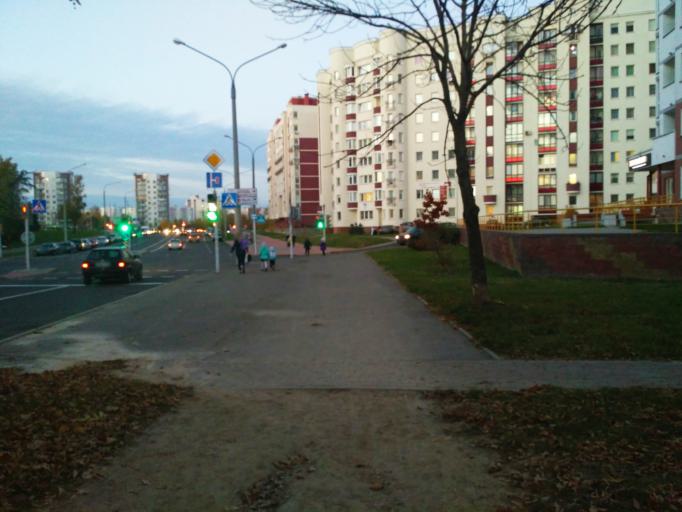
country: BY
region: Minsk
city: Novoye Medvezhino
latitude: 53.8695
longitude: 27.4861
